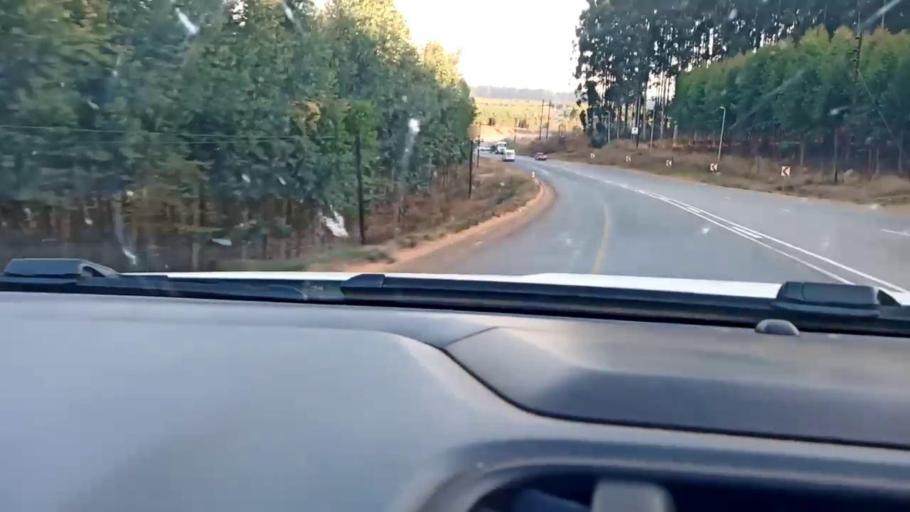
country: ZA
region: Limpopo
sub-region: Mopani District Municipality
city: Duiwelskloof
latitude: -23.7077
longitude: 30.1307
